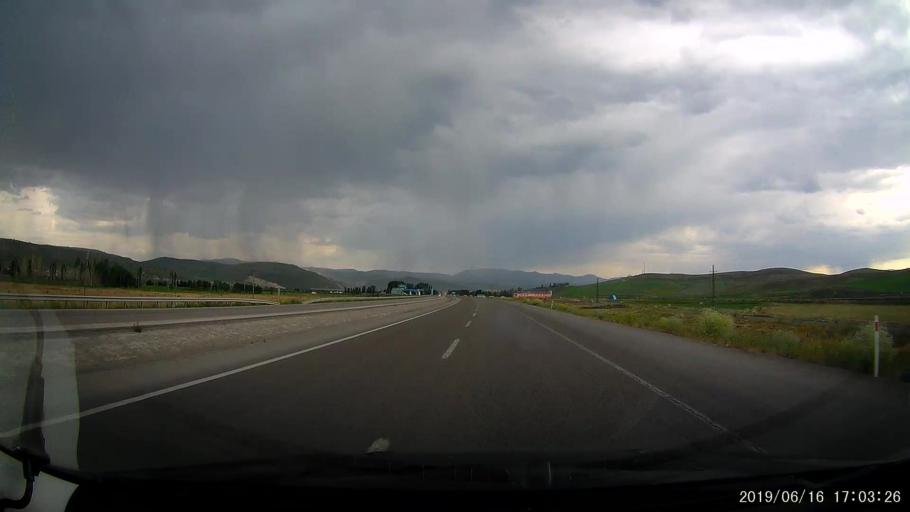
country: TR
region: Erzurum
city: Askale
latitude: 39.9367
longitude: 40.7315
